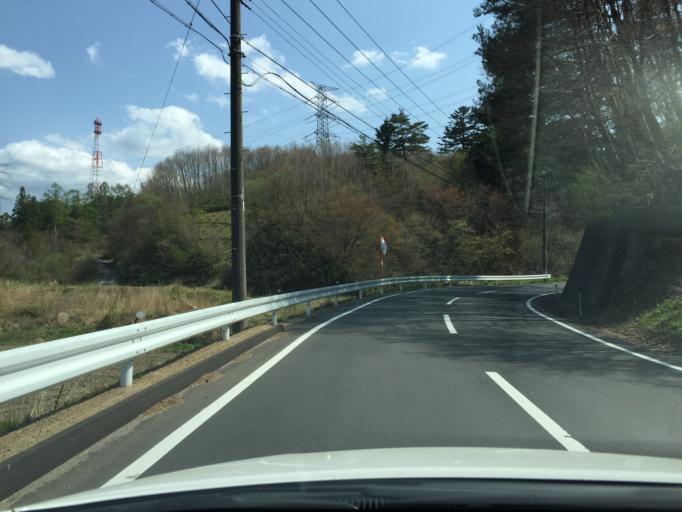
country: JP
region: Fukushima
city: Namie
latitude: 37.3870
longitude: 140.7988
